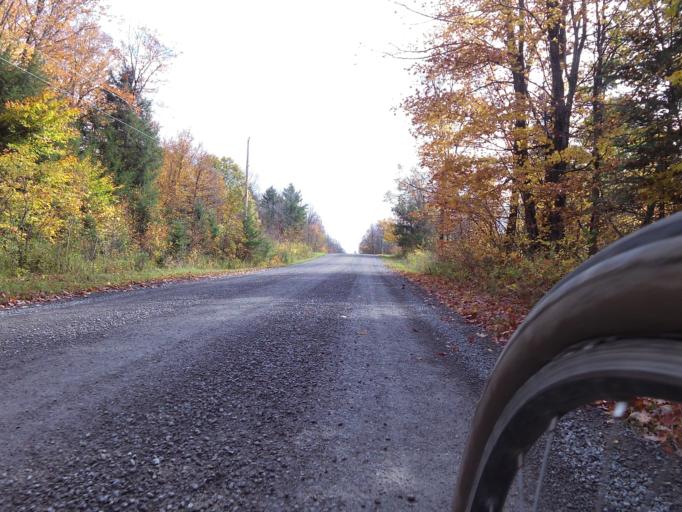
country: CA
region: Ontario
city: Carleton Place
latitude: 45.1526
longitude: -76.2590
